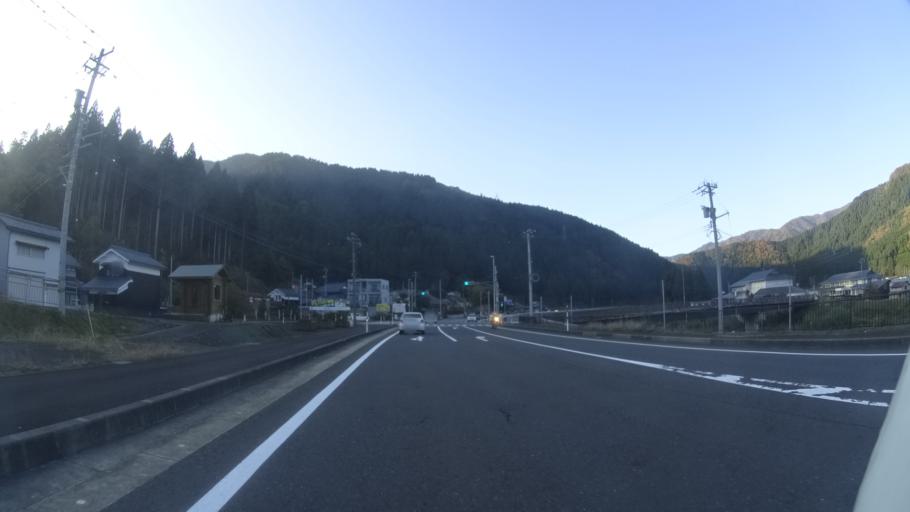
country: JP
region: Fukui
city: Ono
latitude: 35.9976
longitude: 136.3595
